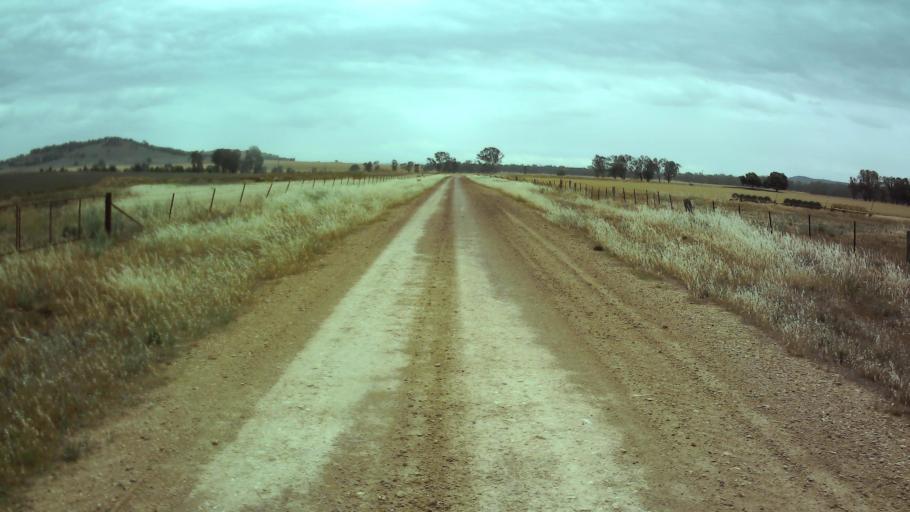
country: AU
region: New South Wales
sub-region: Weddin
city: Grenfell
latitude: -33.9288
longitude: 148.2805
